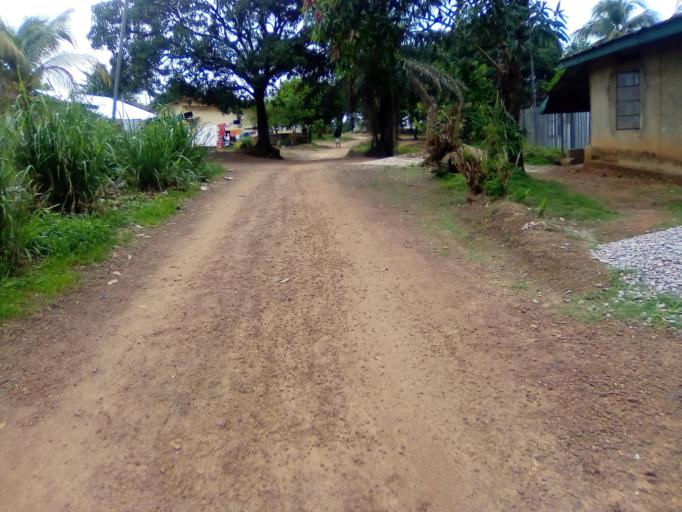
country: SL
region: Southern Province
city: Bo
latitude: 7.9465
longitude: -11.7285
